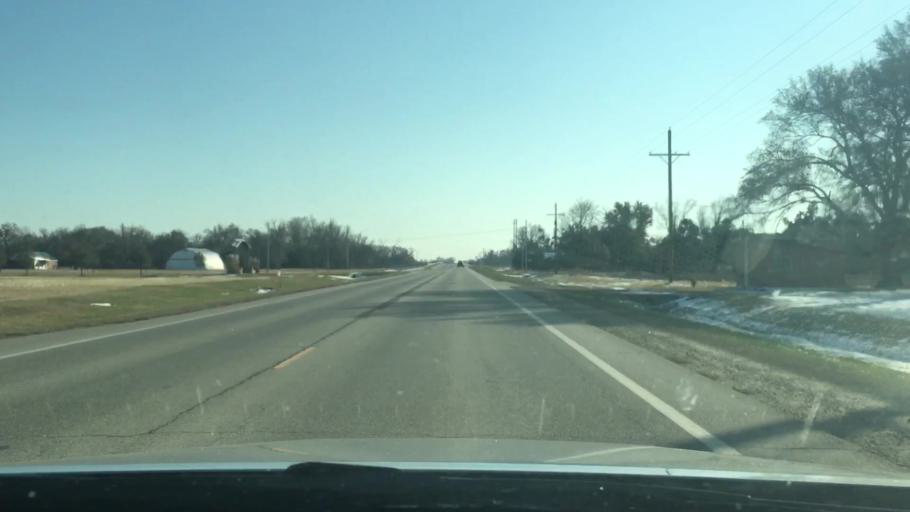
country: US
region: Kansas
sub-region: Rice County
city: Lyons
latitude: 38.3182
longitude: -98.2018
